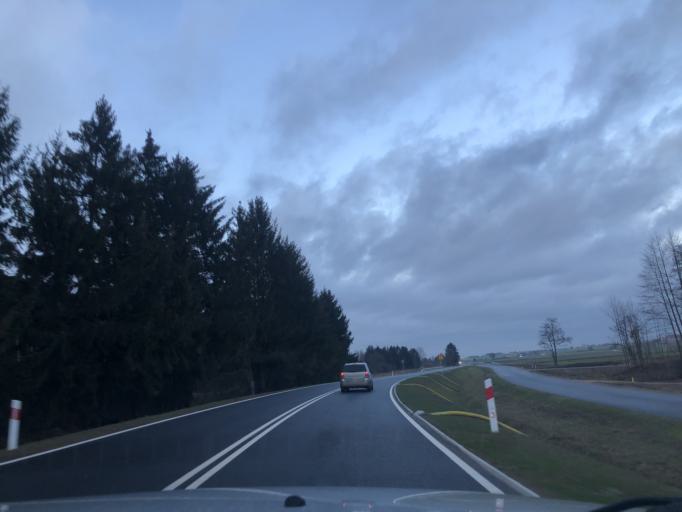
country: PL
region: Podlasie
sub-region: Lomza
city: Lomza
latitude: 53.1282
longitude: 22.0482
